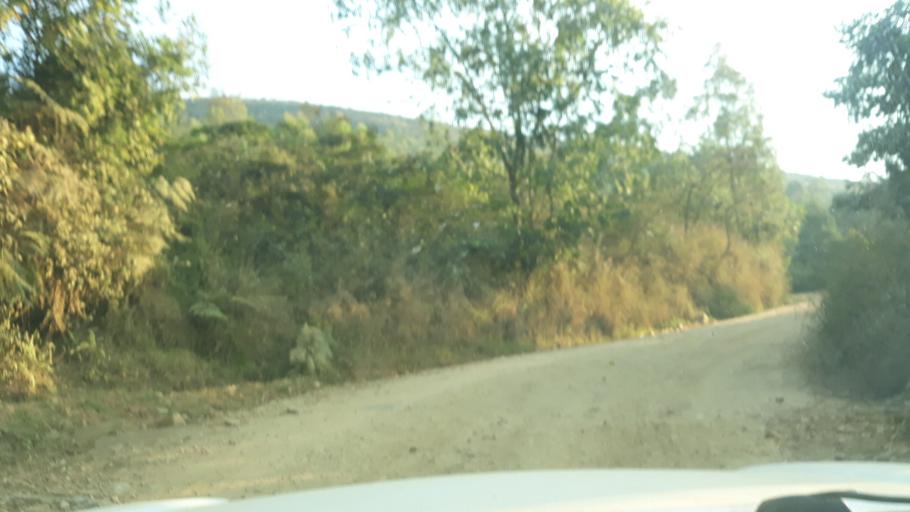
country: RW
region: Western Province
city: Cyangugu
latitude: -2.6987
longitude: 28.9067
